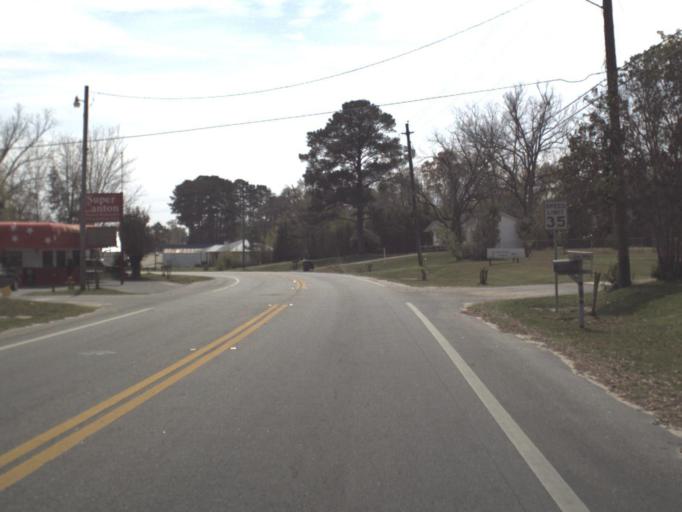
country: US
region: Florida
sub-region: Jackson County
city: Graceville
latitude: 30.9520
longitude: -85.5167
